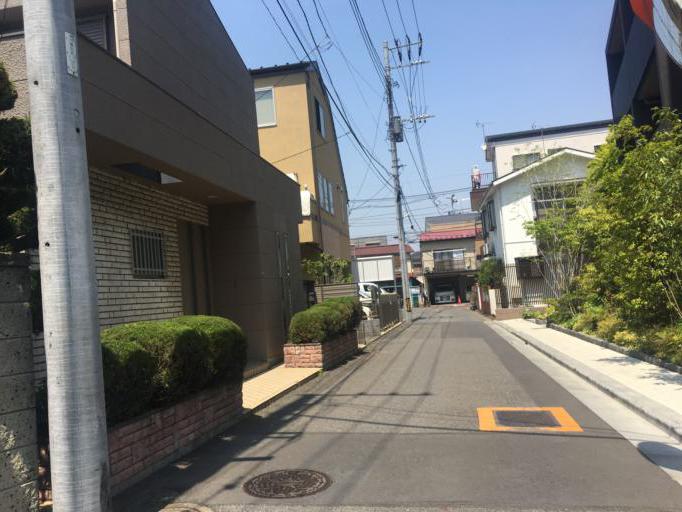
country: JP
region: Saitama
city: Wako
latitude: 35.7785
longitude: 139.6292
